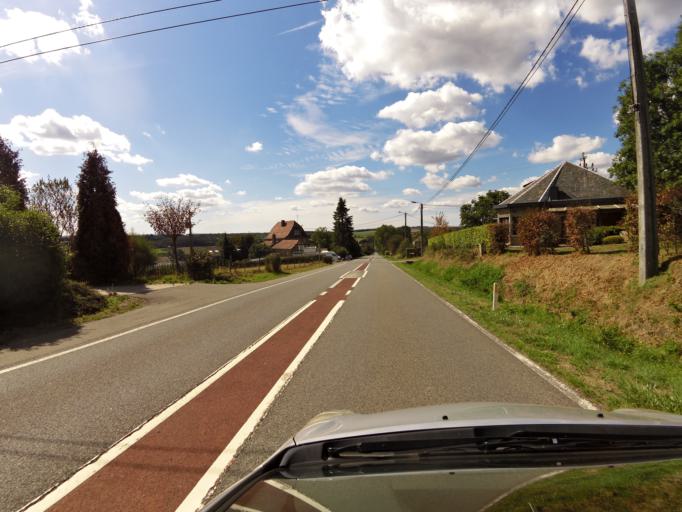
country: BE
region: Wallonia
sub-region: Province de Namur
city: Somme-Leuze
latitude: 50.3427
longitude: 5.3717
